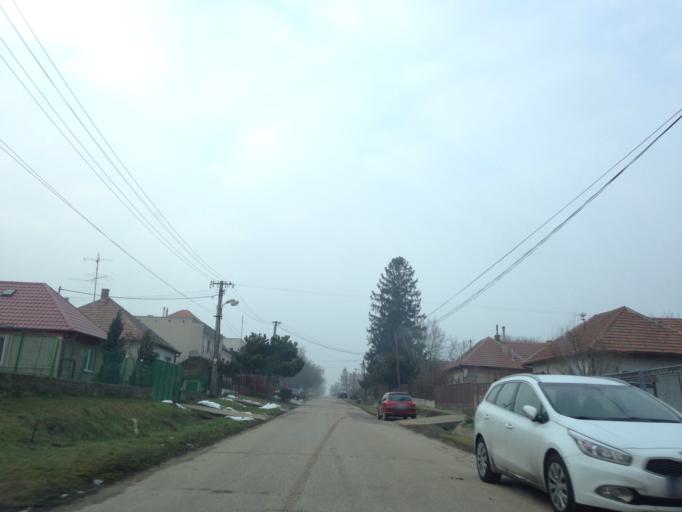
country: SK
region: Nitriansky
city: Svodin
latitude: 47.9940
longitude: 18.3887
